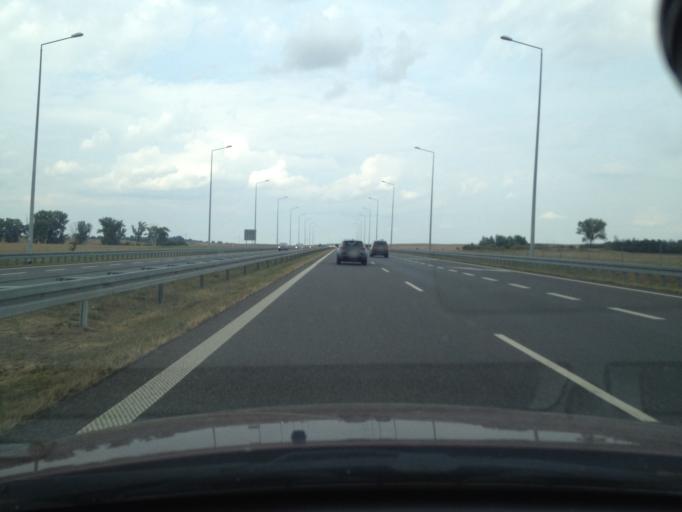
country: PL
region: West Pomeranian Voivodeship
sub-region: Powiat pyrzycki
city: Kozielice
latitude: 53.0547
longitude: 14.8651
